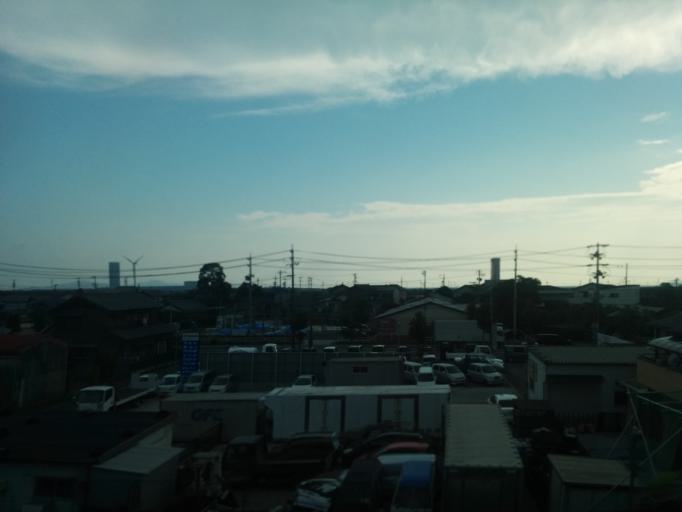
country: JP
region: Aichi
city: Kozakai-cho
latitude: 34.8054
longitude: 137.3136
